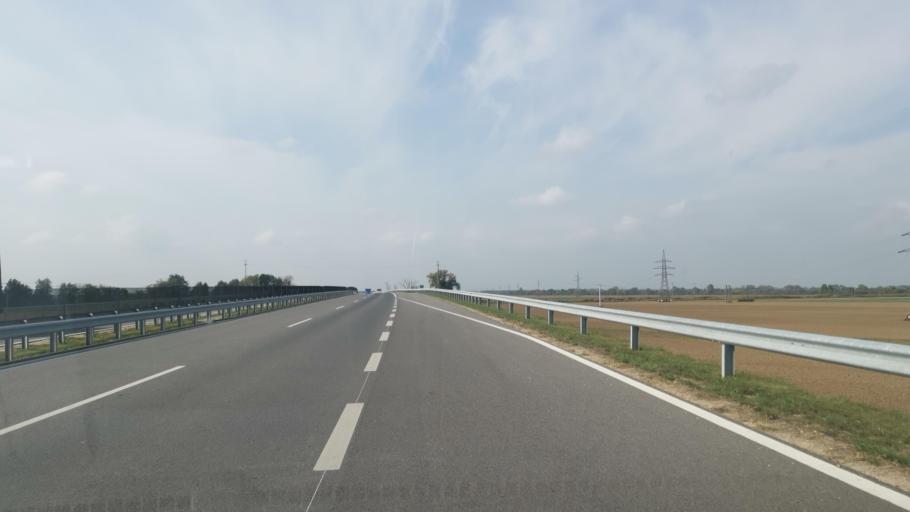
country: HU
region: Gyor-Moson-Sopron
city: Kapuvar
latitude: 47.5702
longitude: 17.0421
